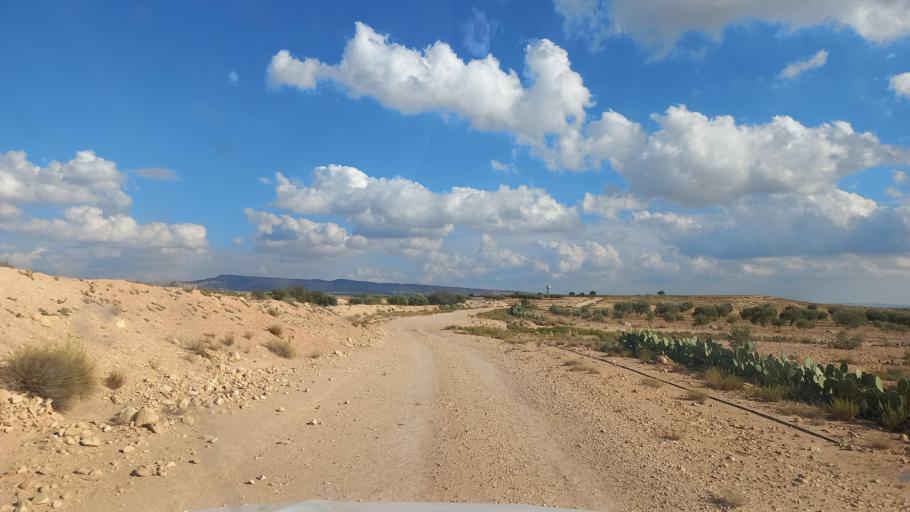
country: TN
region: Al Qasrayn
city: Sbiba
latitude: 35.3973
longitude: 9.0378
